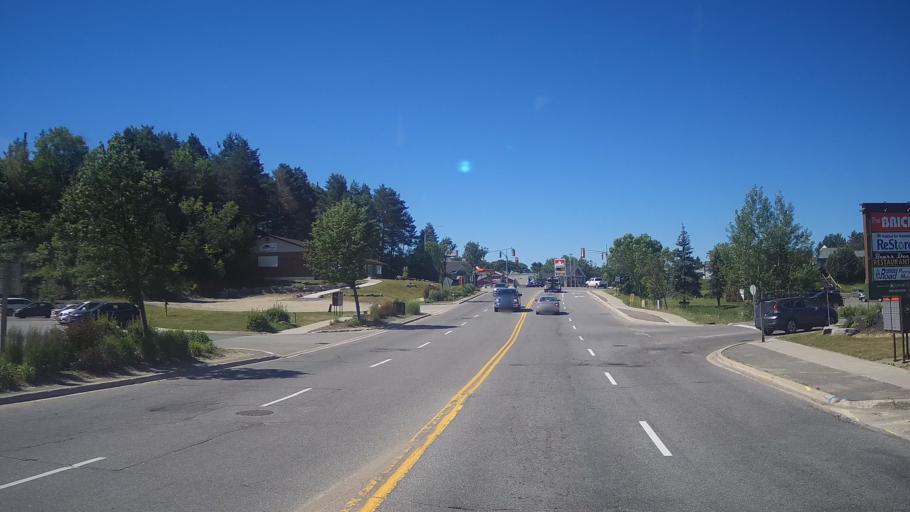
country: CA
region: Ontario
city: Huntsville
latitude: 45.3344
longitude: -79.2057
